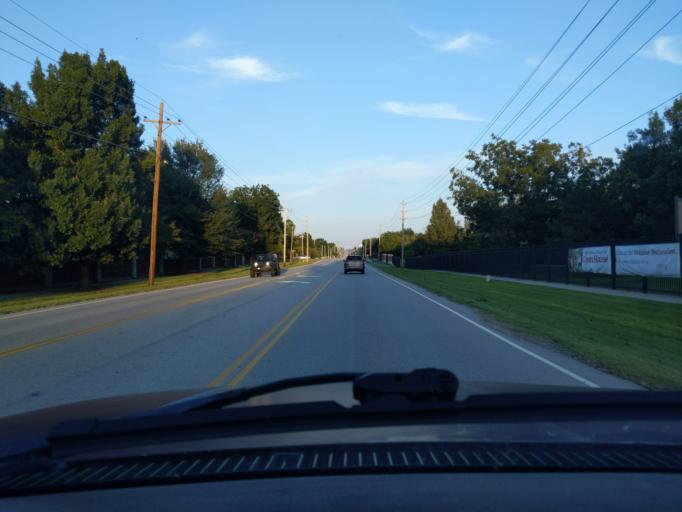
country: US
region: Oklahoma
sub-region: Tulsa County
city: Jenks
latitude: 36.0463
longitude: -95.9147
